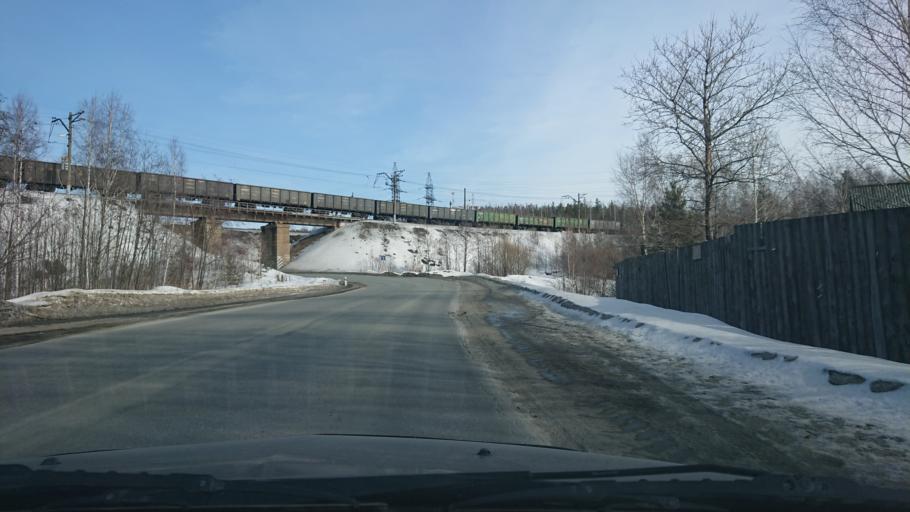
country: RU
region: Sverdlovsk
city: Revda
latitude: 56.8202
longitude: 59.9767
